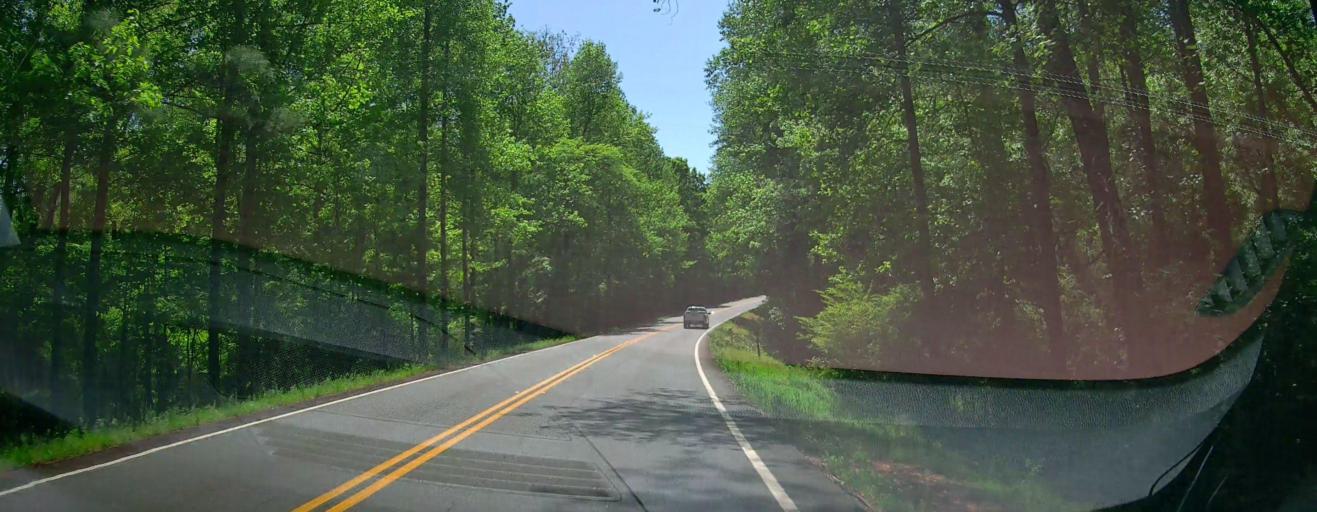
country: US
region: Georgia
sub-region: Jasper County
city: Monticello
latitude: 33.2841
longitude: -83.6470
